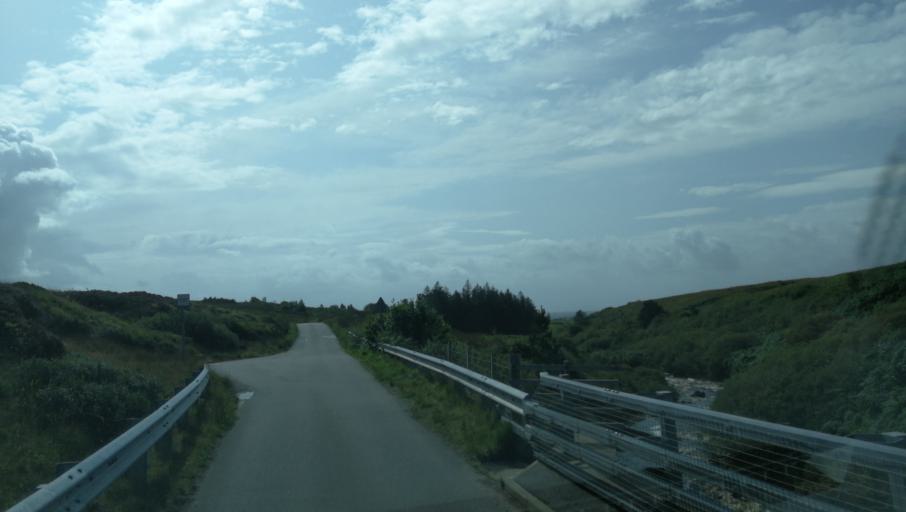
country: GB
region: Scotland
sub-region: Highland
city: Portree
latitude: 57.7481
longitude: -5.7624
